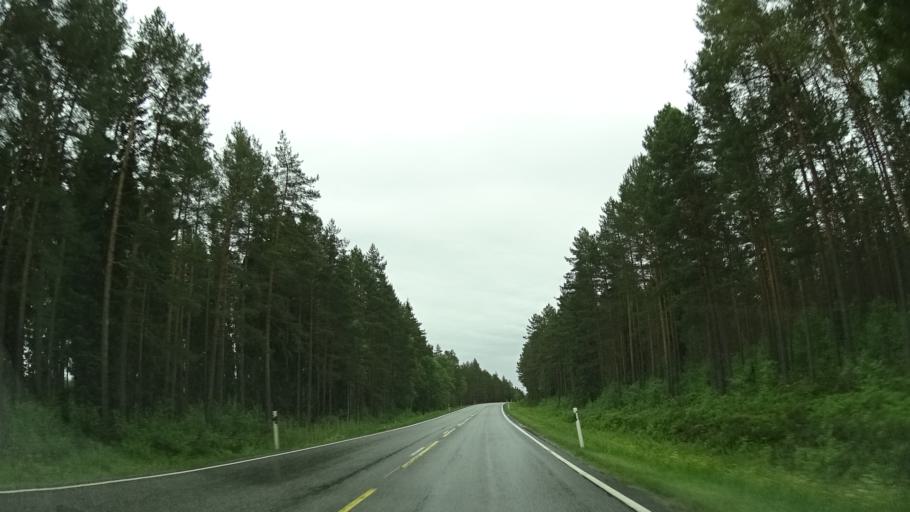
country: FI
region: Varsinais-Suomi
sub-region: Salo
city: Pernioe
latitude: 60.1123
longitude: 23.2131
